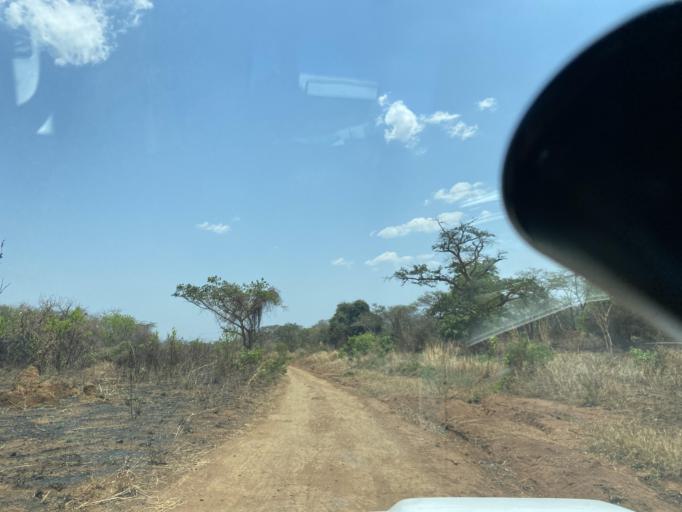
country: ZM
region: Lusaka
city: Lusaka
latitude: -15.5057
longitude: 28.0092
